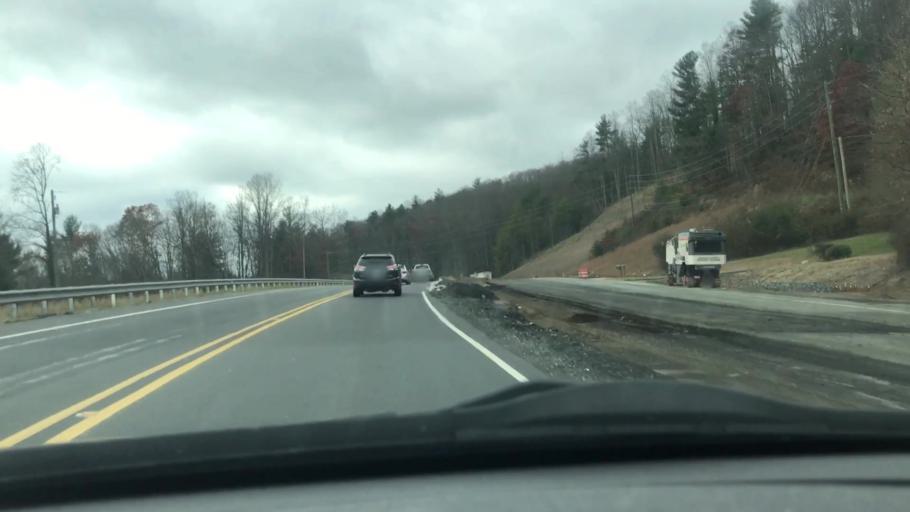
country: US
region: North Carolina
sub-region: Mitchell County
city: Spruce Pine
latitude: 35.9118
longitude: -82.0944
